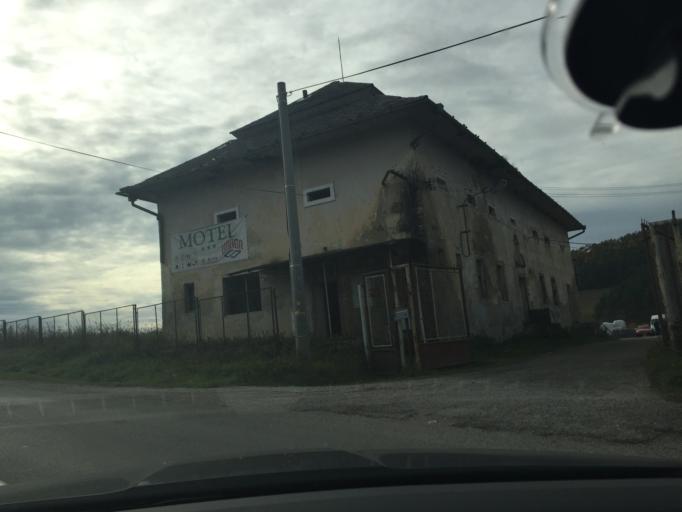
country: SK
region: Presovsky
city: Spisske Podhradie
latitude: 48.9691
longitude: 20.7837
